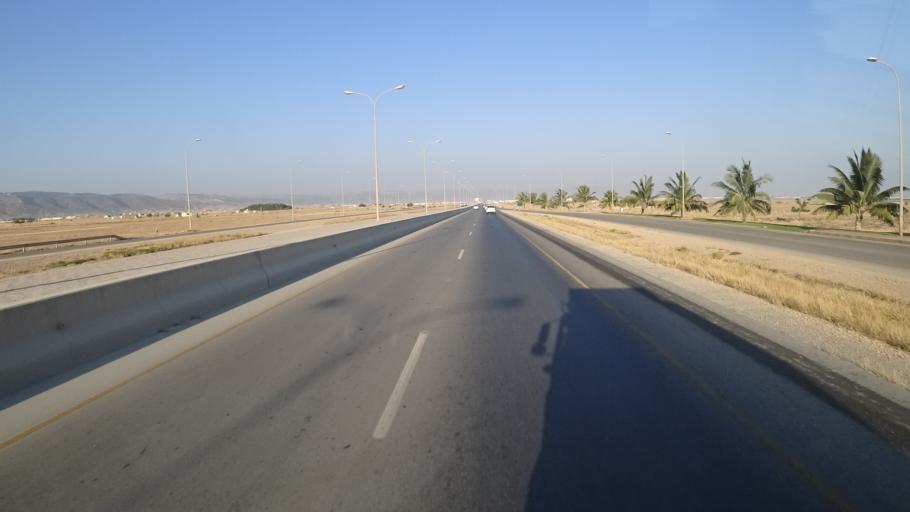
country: OM
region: Zufar
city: Salalah
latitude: 17.0619
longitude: 54.0876
